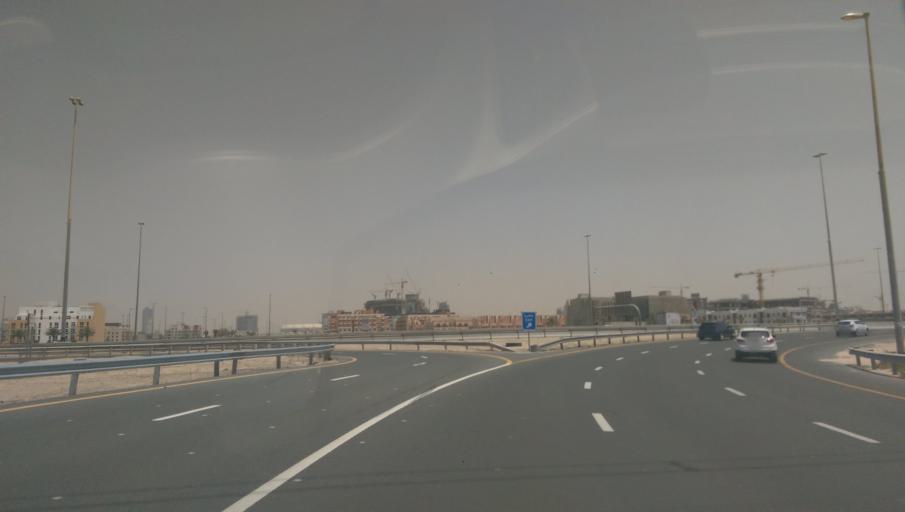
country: AE
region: Dubai
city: Dubai
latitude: 25.0643
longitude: 55.1977
